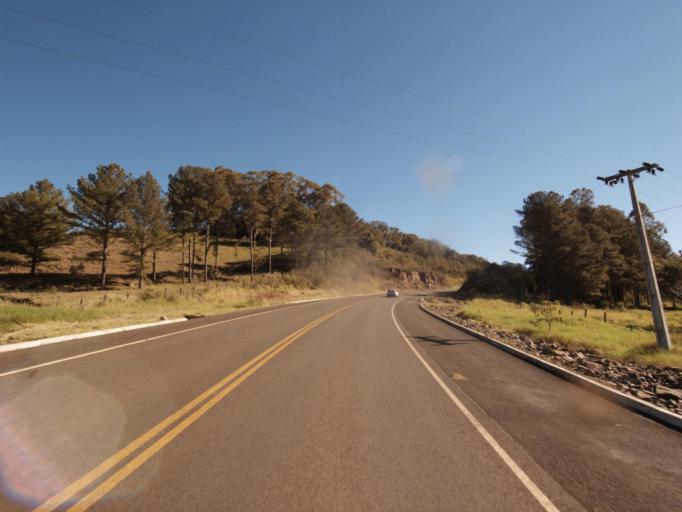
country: AR
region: Misiones
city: Bernardo de Irigoyen
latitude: -26.6183
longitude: -53.6589
